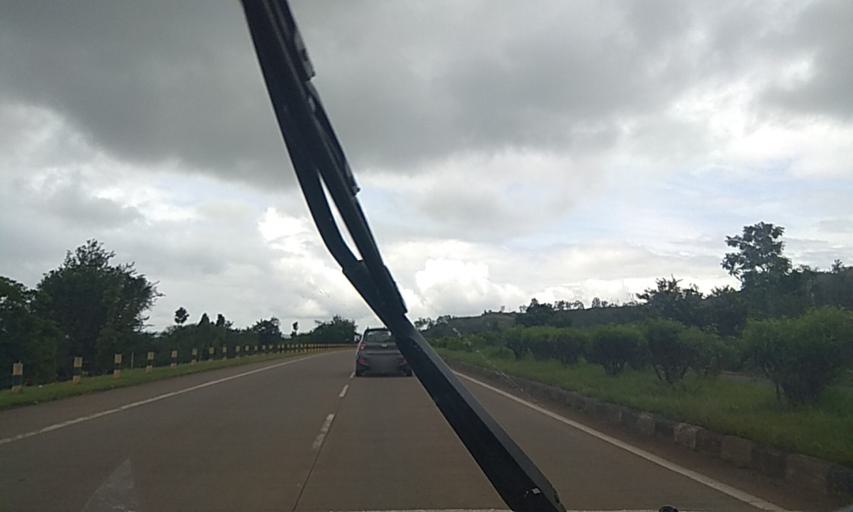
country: IN
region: Karnataka
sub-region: Belgaum
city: Sankeshwar
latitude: 16.2832
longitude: 74.4459
